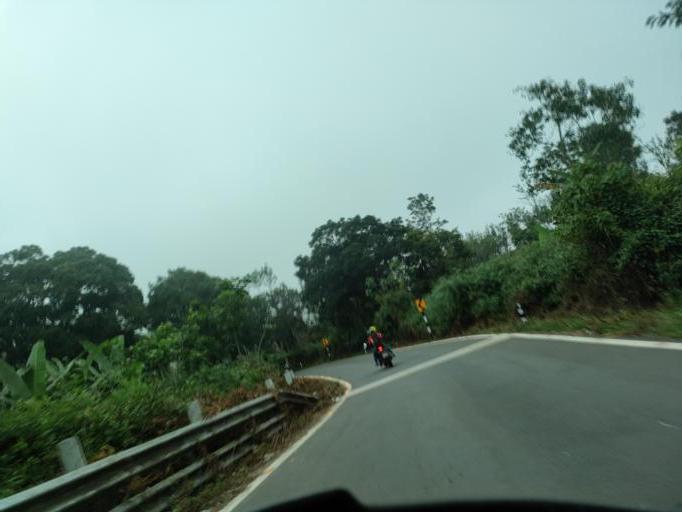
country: IN
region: Tamil Nadu
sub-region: Dindigul
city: Ayakudi
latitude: 10.3377
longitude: 77.5624
